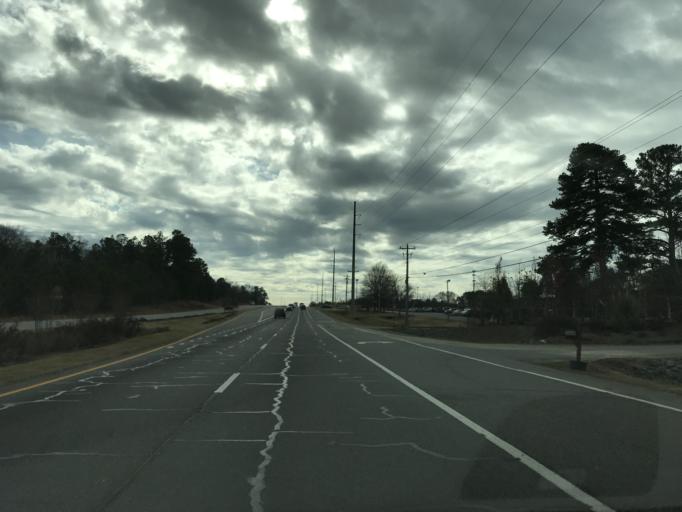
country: US
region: Georgia
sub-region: Fulton County
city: Johns Creek
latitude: 34.1143
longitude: -84.1766
